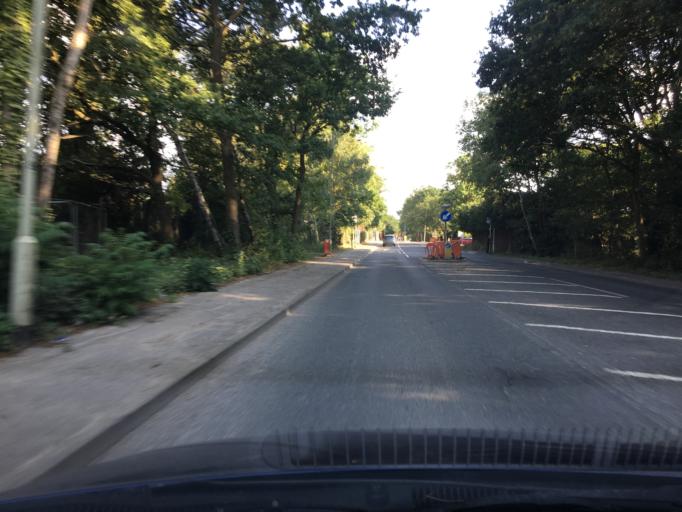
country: GB
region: England
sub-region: Bracknell Forest
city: Crowthorne
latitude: 51.3803
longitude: -0.7915
